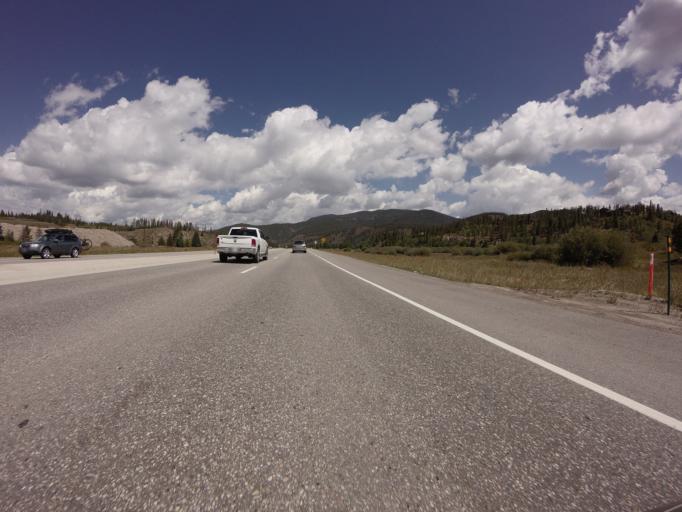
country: US
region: Colorado
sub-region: Summit County
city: Breckenridge
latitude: 39.5358
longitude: -106.0427
